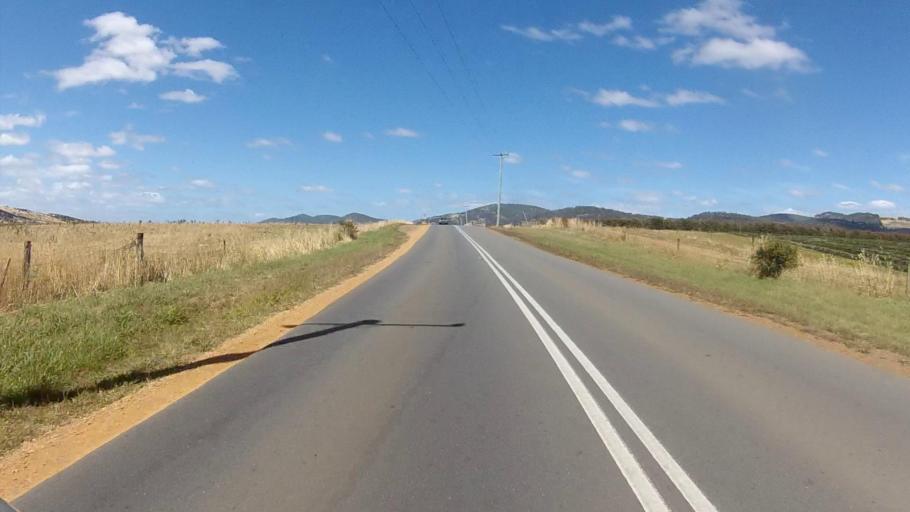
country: AU
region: Tasmania
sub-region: Clarence
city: Cambridge
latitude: -42.7556
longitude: 147.4158
